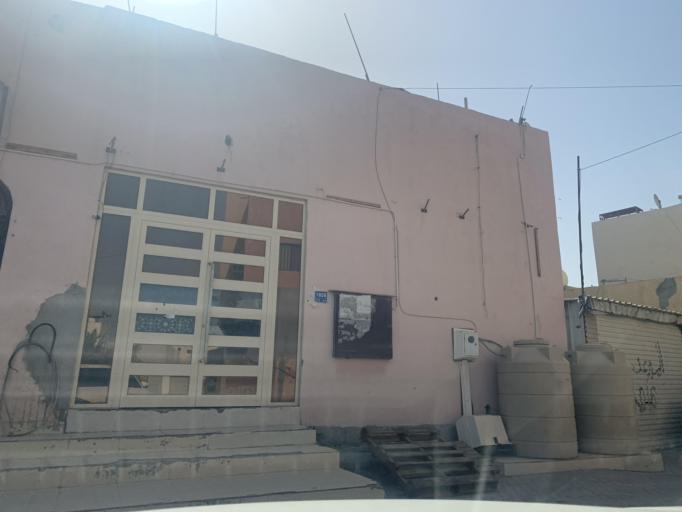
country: BH
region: Northern
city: Sitrah
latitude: 26.1673
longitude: 50.6258
